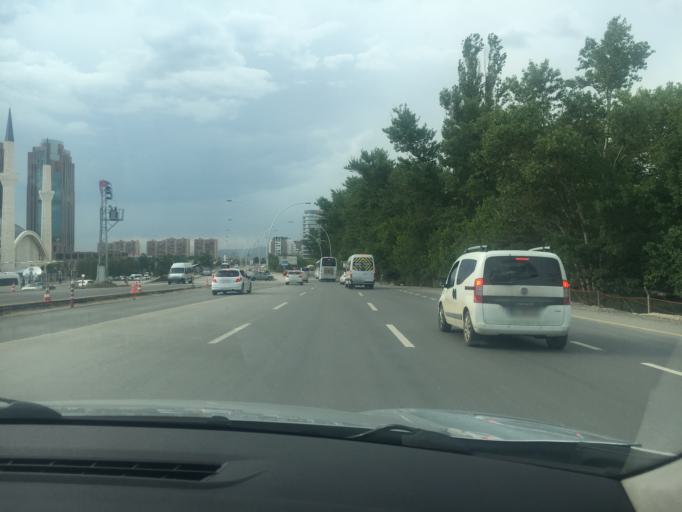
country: TR
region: Ankara
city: Batikent
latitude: 39.9044
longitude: 32.7652
